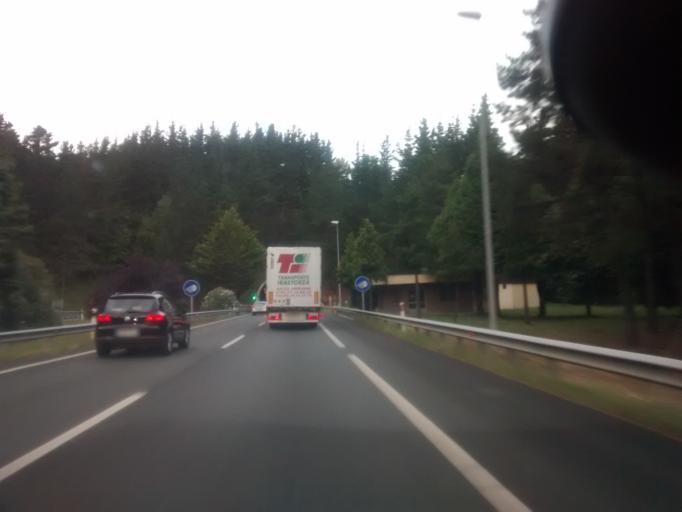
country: ES
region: Basque Country
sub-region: Provincia de Guipuzcoa
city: Deba
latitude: 43.2846
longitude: -2.3350
